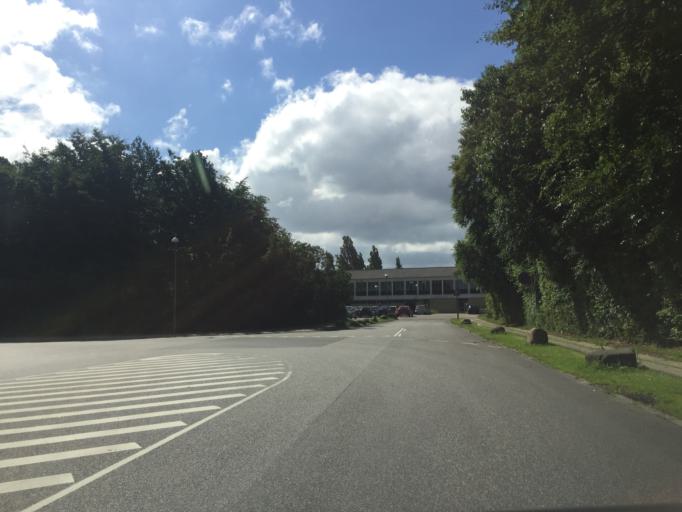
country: DK
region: Capital Region
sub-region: Brondby Kommune
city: Brondbyvester
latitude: 55.6551
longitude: 12.4191
